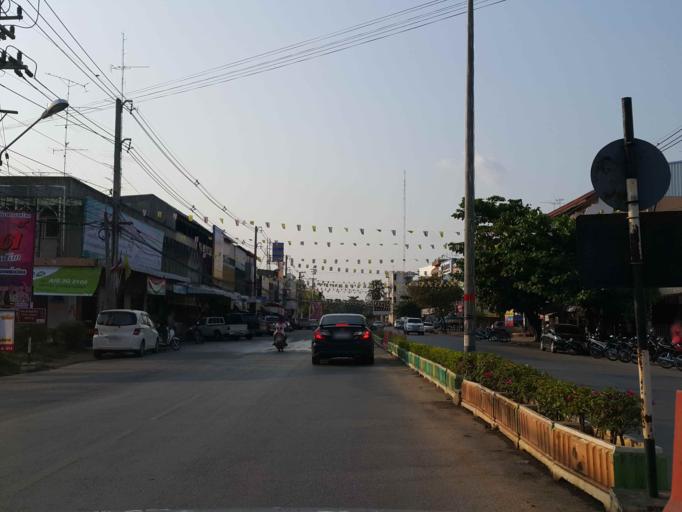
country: TH
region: Sukhothai
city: Sawankhalok
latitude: 17.3101
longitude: 99.8310
